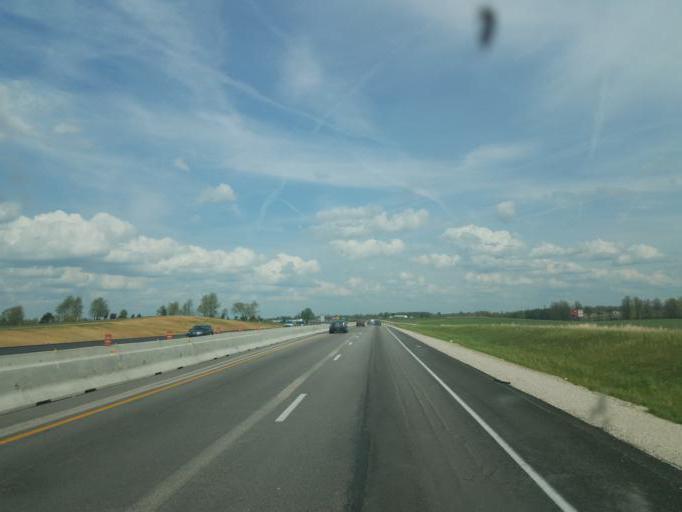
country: US
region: Kentucky
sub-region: Larue County
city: Hodgenville
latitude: 37.4858
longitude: -85.8805
